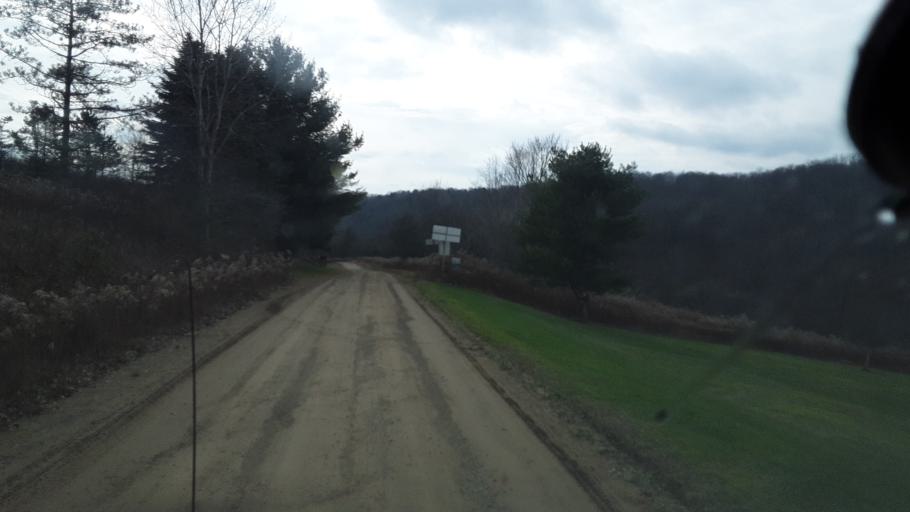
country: US
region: Pennsylvania
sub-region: Tioga County
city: Westfield
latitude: 41.9137
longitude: -77.7187
